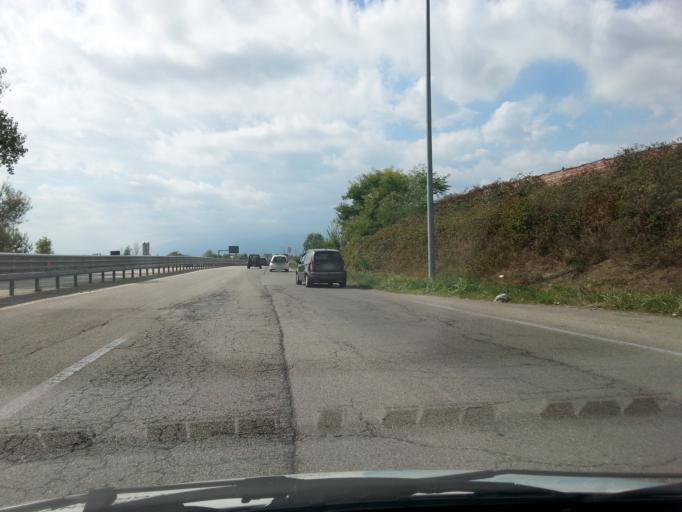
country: IT
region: Piedmont
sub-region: Provincia di Torino
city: Riva
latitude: 44.8864
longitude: 7.3575
